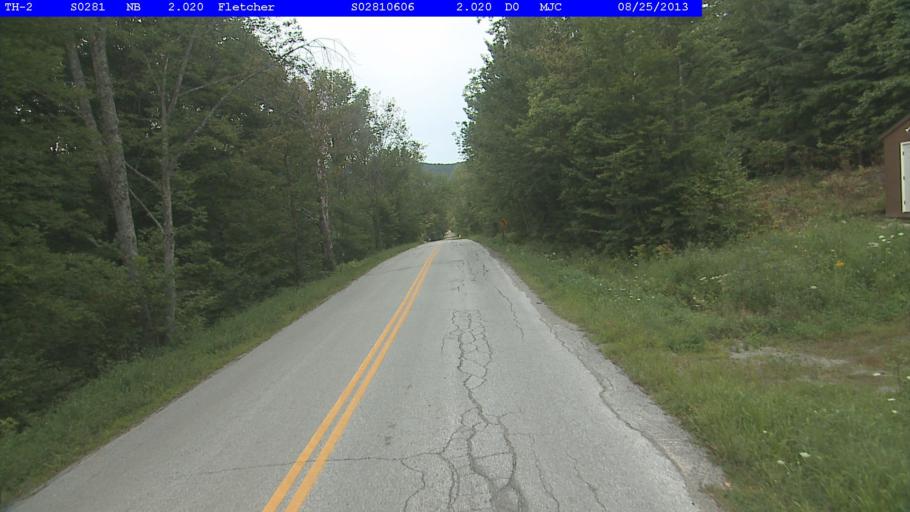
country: US
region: Vermont
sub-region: Franklin County
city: Saint Albans
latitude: 44.7034
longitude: -72.9375
